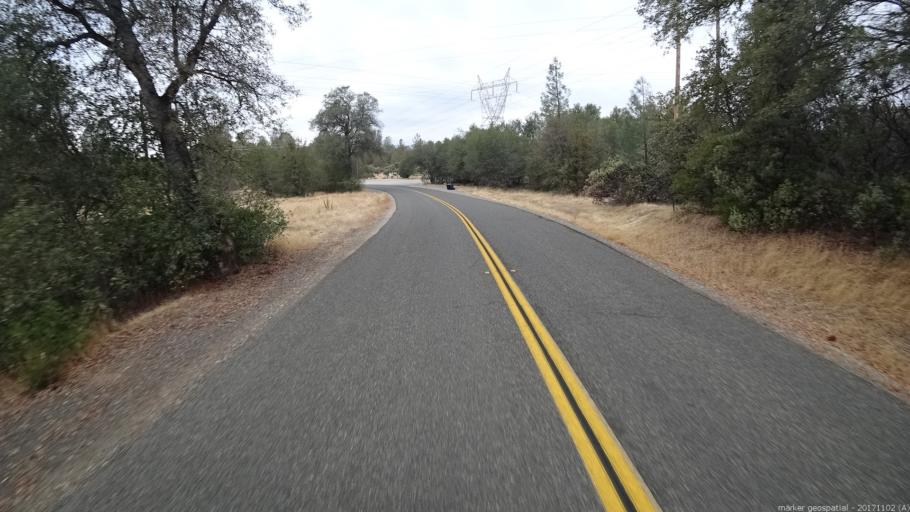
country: US
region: California
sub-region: Shasta County
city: Redding
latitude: 40.6353
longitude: -122.4210
